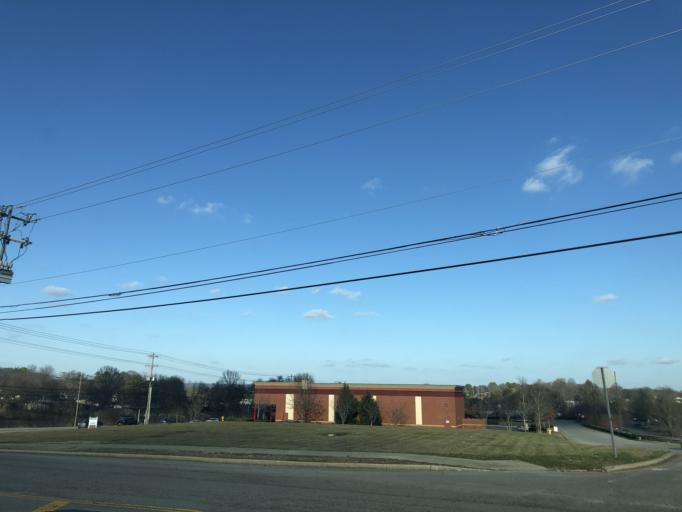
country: US
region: Tennessee
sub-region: Sumner County
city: Gallatin
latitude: 36.3655
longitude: -86.4893
